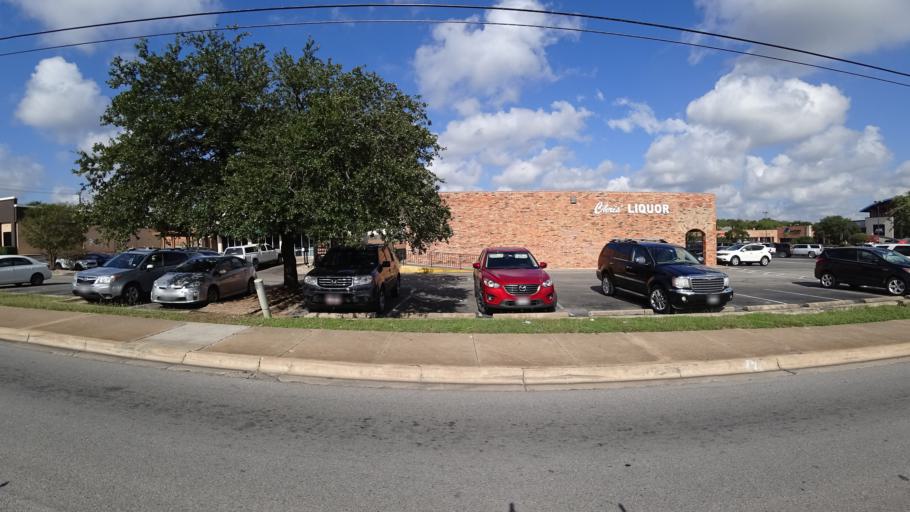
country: US
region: Texas
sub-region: Travis County
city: Shady Hollow
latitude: 30.2083
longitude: -97.8156
